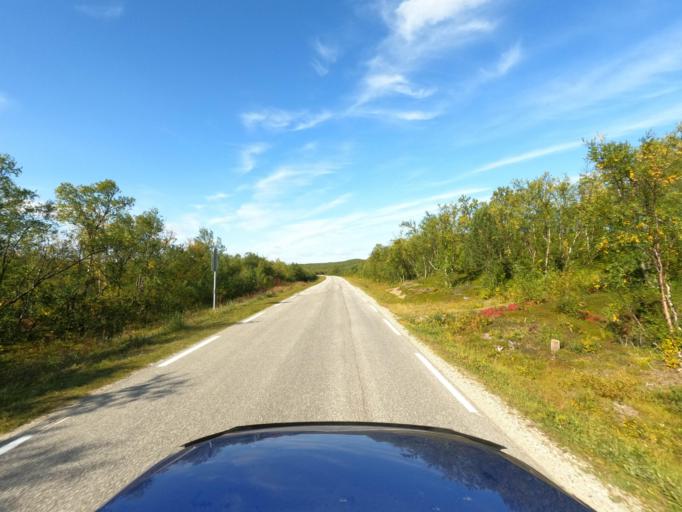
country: NO
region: Finnmark Fylke
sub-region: Porsanger
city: Lakselv
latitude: 69.7567
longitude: 25.2127
